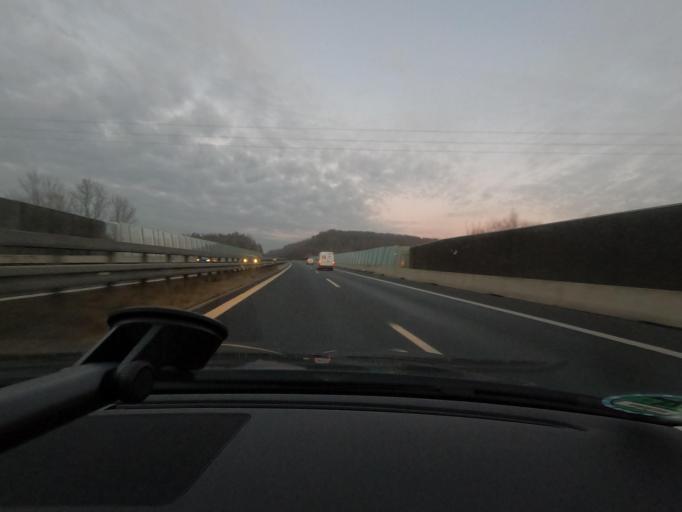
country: DE
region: Bavaria
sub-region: Upper Franconia
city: Zapfendorf
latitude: 50.0076
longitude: 10.9344
